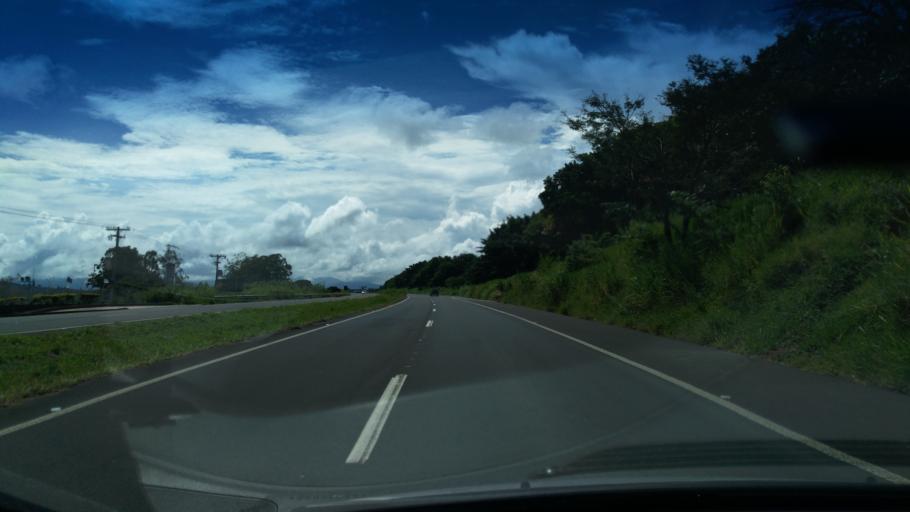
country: BR
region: Sao Paulo
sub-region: Santo Antonio Do Jardim
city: Espirito Santo do Pinhal
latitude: -22.1786
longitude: -46.7525
